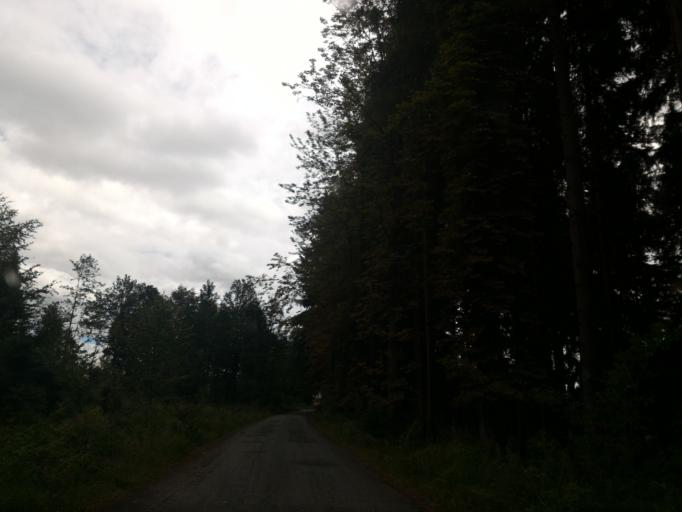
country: CZ
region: Vysocina
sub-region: Okres Jihlava
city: Telc
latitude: 49.2467
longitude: 15.4257
